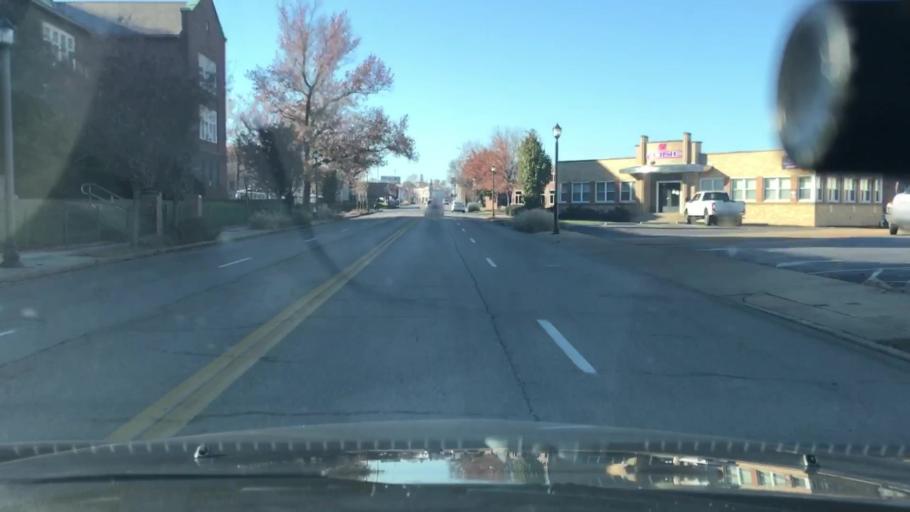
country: US
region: Missouri
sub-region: Saint Louis County
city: Richmond Heights
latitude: 38.6158
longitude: -90.2634
